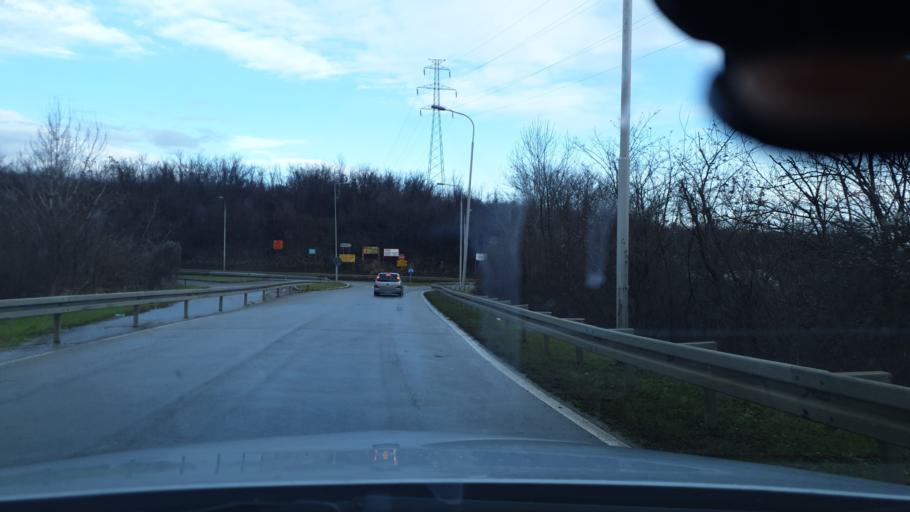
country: RS
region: Central Serbia
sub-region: Podunavski Okrug
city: Smederevo
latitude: 44.6087
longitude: 20.9560
